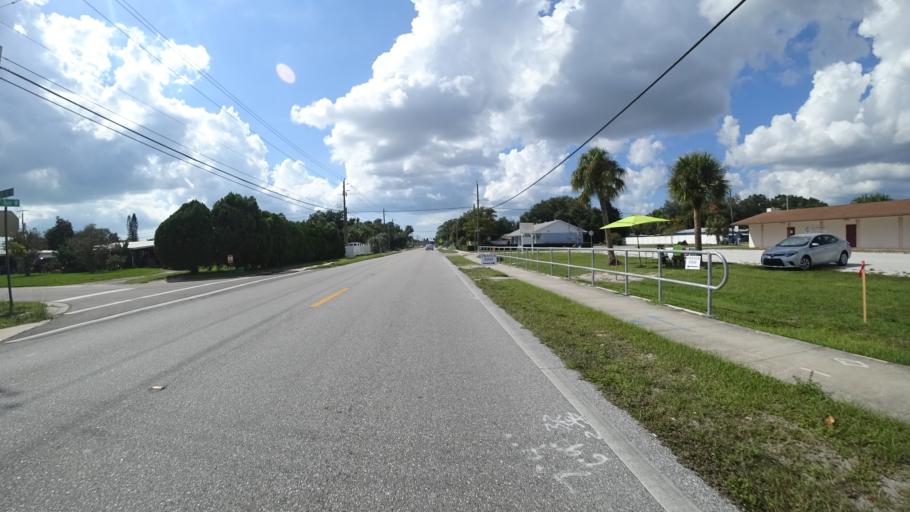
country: US
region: Florida
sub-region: Manatee County
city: Bayshore Gardens
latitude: 27.4404
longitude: -82.5850
